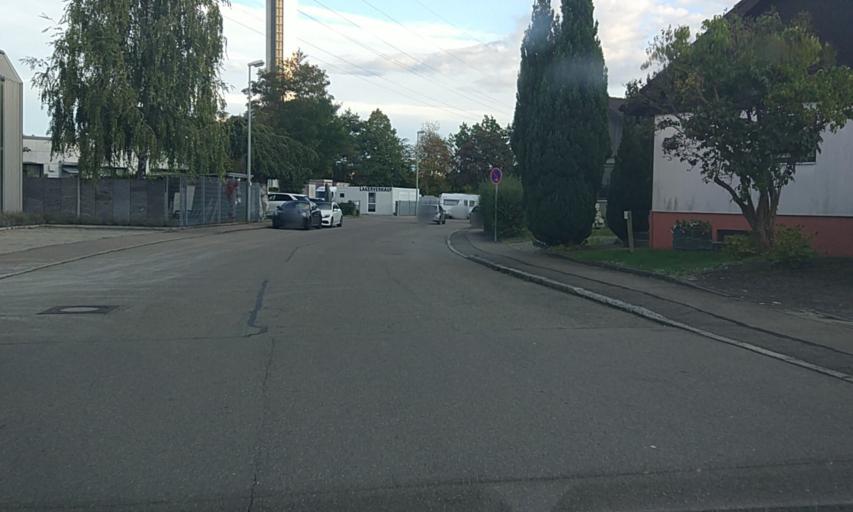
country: DE
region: Baden-Wuerttemberg
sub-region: Tuebingen Region
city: Ulm
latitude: 48.4342
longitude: 9.9759
